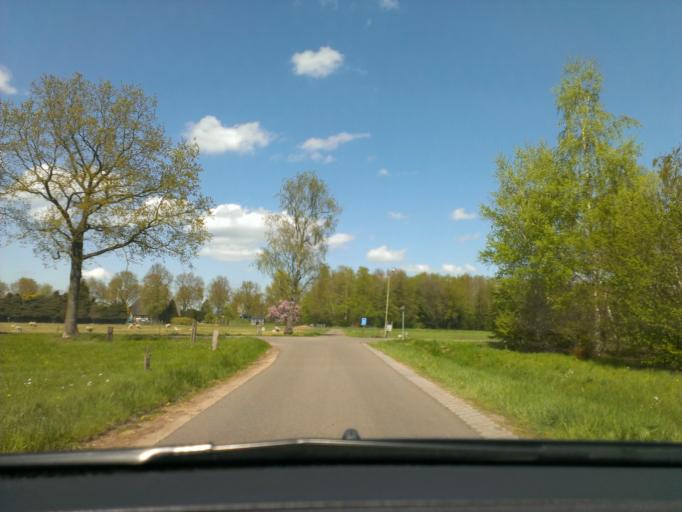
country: NL
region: Gelderland
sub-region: Gemeente Epe
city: Epe
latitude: 52.3336
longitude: 5.9989
